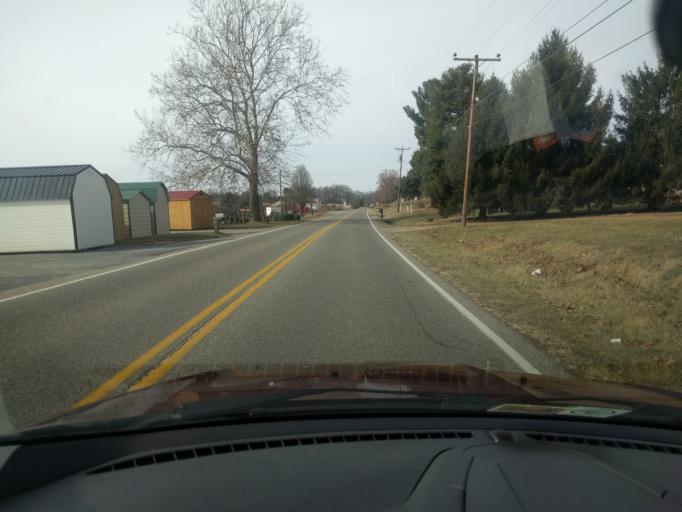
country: US
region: Virginia
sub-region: Augusta County
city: Stuarts Draft
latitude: 38.0314
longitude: -79.0613
